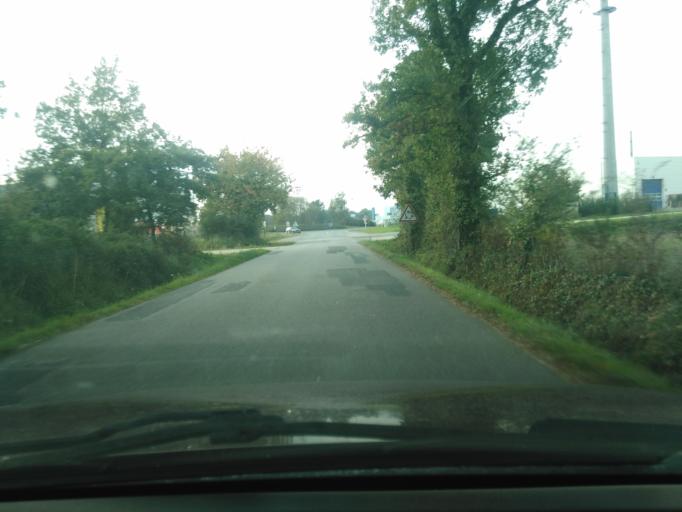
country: FR
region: Pays de la Loire
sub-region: Departement de la Vendee
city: Mouilleron-le-Captif
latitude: 46.7128
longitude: -1.4256
